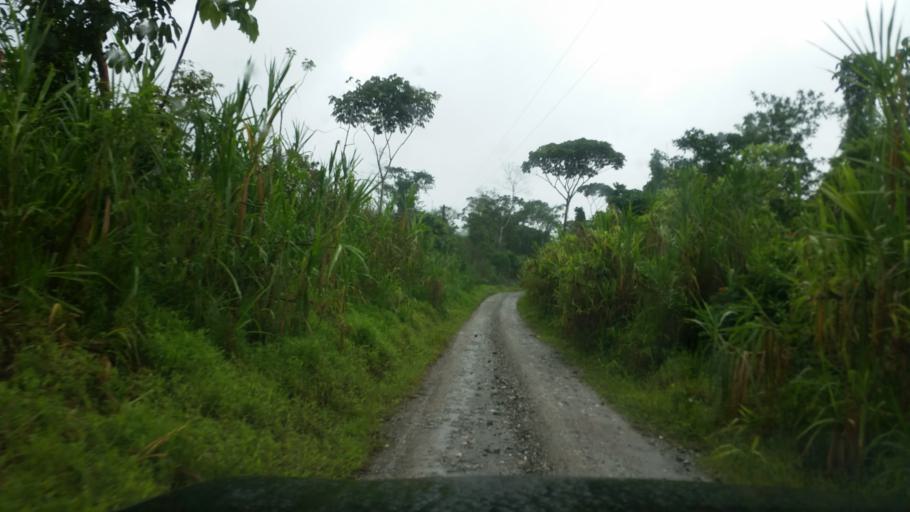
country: NI
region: Atlantico Norte (RAAN)
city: Bonanza
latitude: 14.0763
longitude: -84.6572
